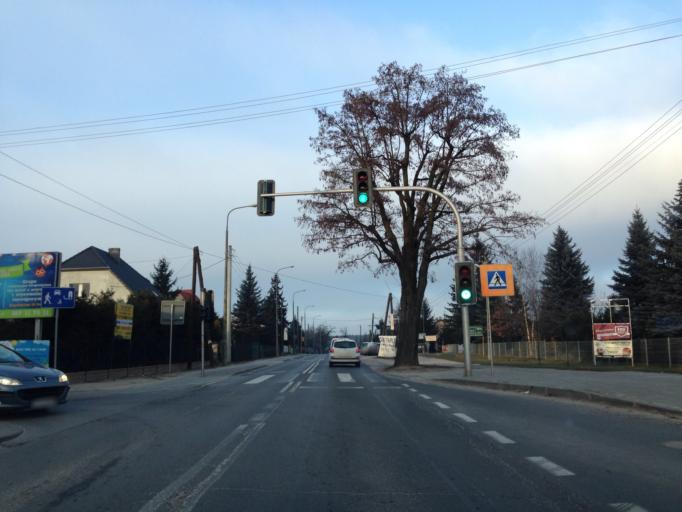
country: PL
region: Greater Poland Voivodeship
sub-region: Powiat poznanski
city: Czerwonak
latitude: 52.4555
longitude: 16.9476
